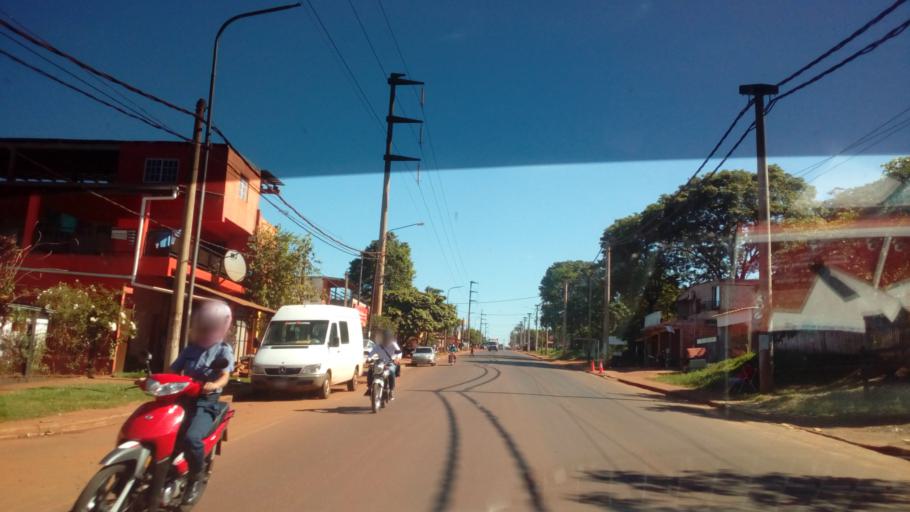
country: AR
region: Misiones
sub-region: Departamento de Capital
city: Posadas
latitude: -27.4233
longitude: -55.9137
